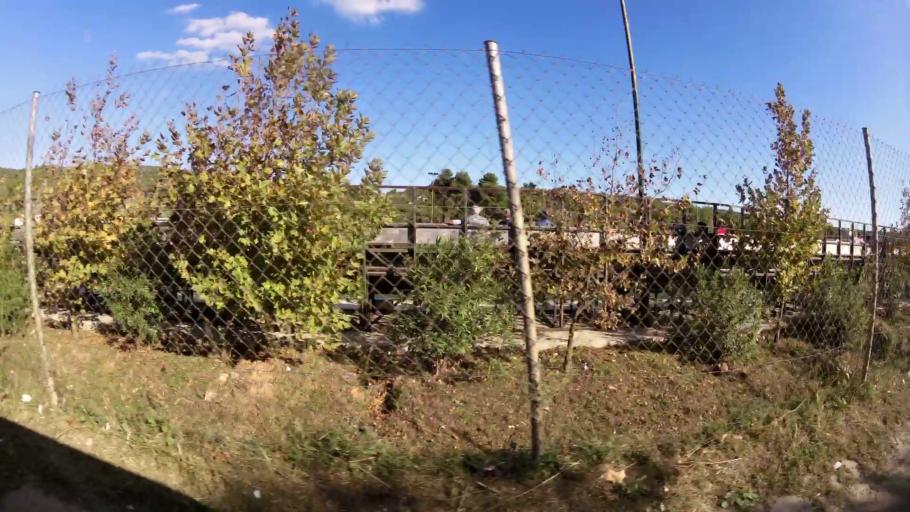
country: GR
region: Attica
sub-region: Nomarchia Anatolikis Attikis
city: Anthousa
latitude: 38.0372
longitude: 23.8821
